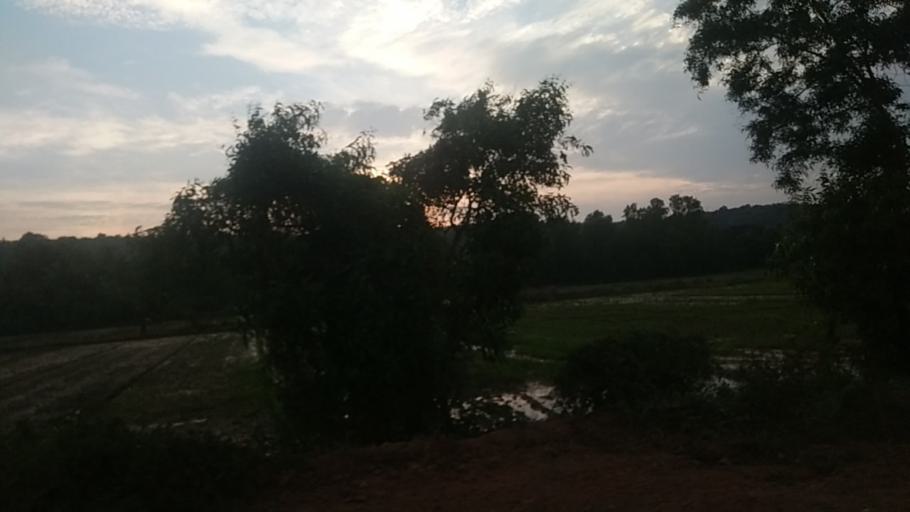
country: IN
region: Goa
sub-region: South Goa
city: Cortalim
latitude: 15.3933
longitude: 73.9145
